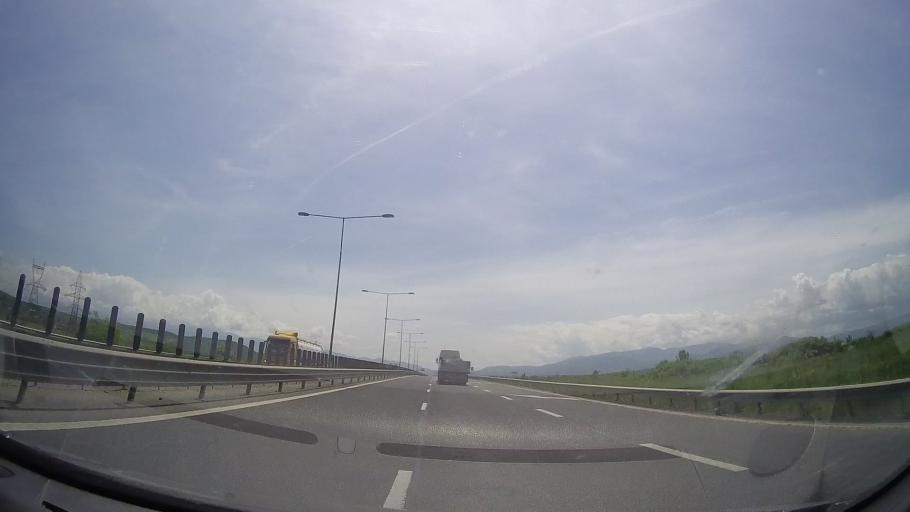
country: RO
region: Sibiu
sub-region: Comuna Selimbar
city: Selimbar
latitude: 45.7844
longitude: 24.2007
